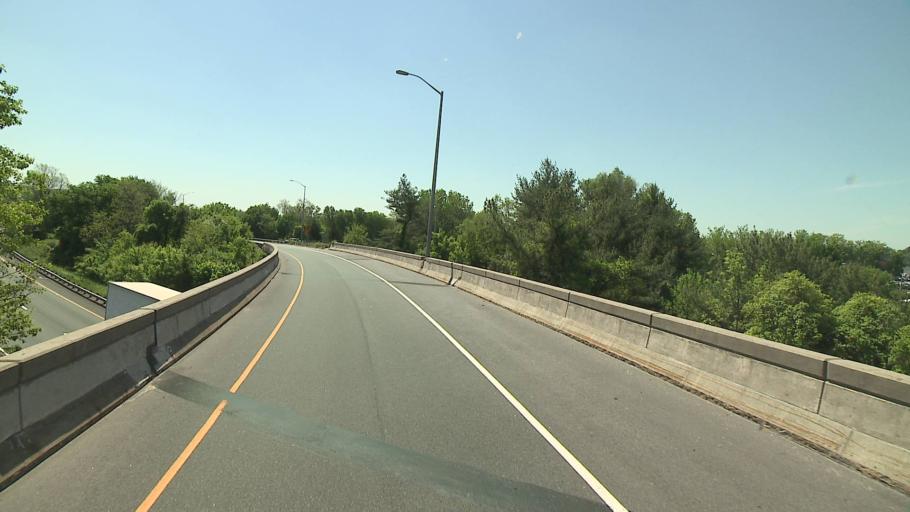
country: US
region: Connecticut
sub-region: Fairfield County
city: Danbury
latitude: 41.4184
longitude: -73.4223
